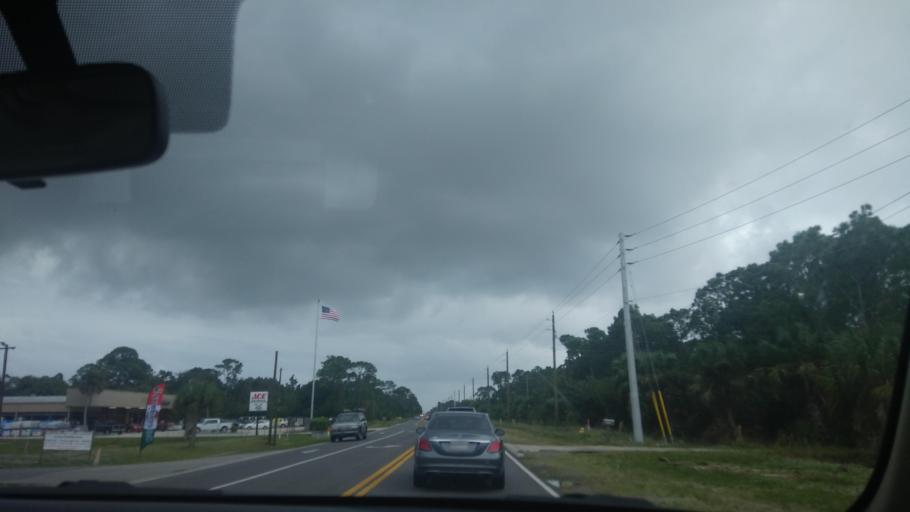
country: US
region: Florida
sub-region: Brevard County
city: Malabar
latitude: 27.9802
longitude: -80.6225
